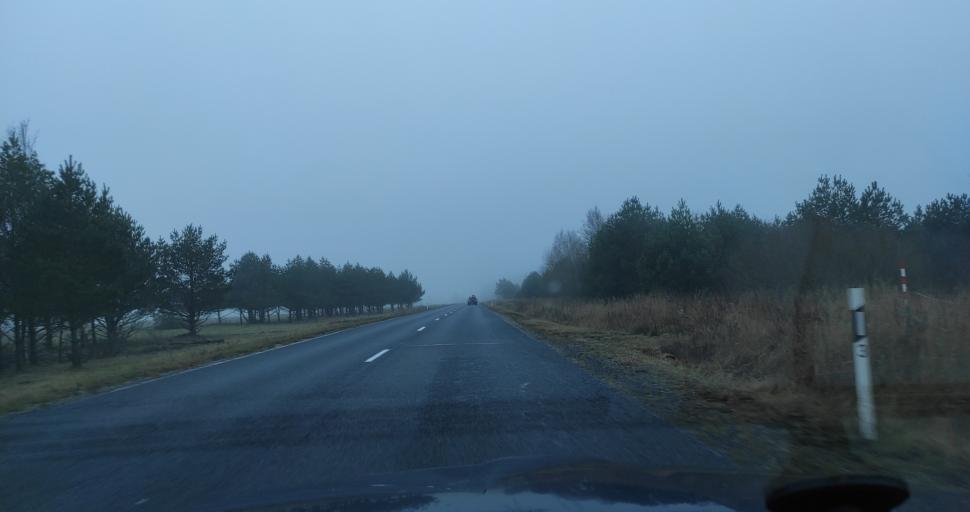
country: LV
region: Alsunga
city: Alsunga
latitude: 57.1124
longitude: 21.4228
